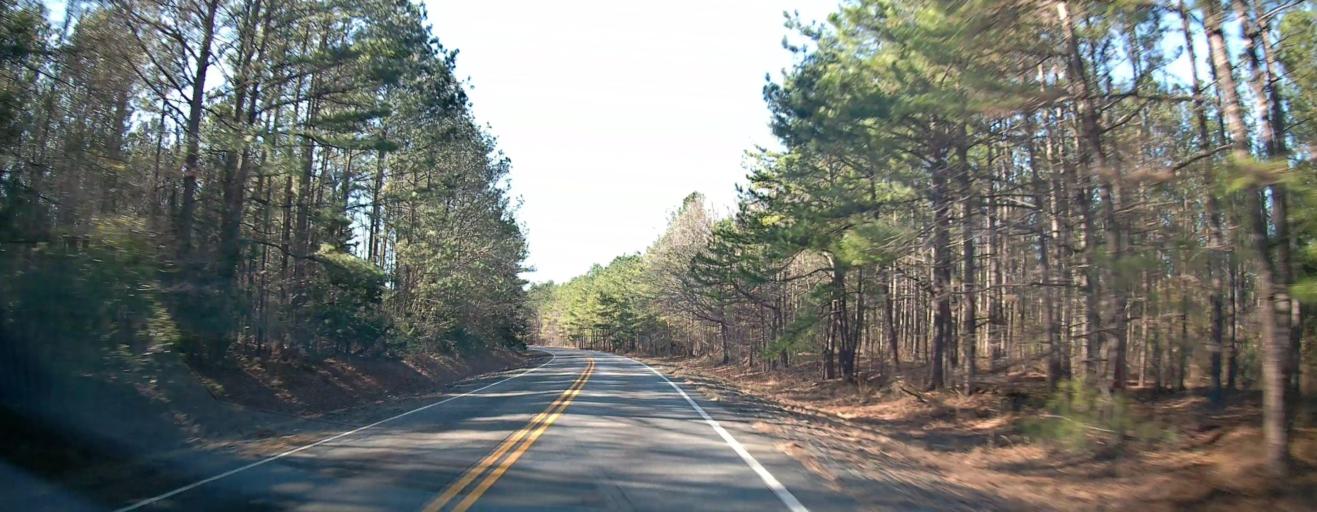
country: US
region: Georgia
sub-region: Talbot County
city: Talbotton
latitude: 32.6494
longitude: -84.4433
